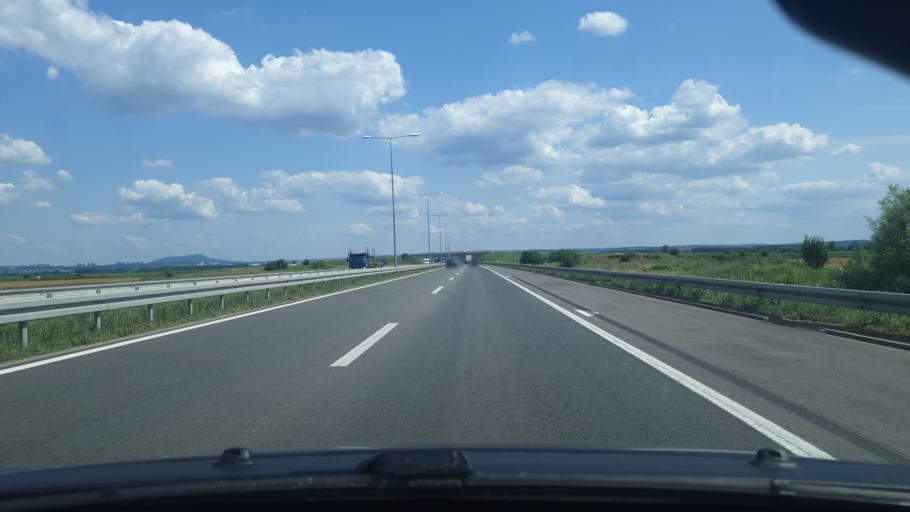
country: RS
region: Central Serbia
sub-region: Belgrade
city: Surcin
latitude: 44.7624
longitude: 20.2849
